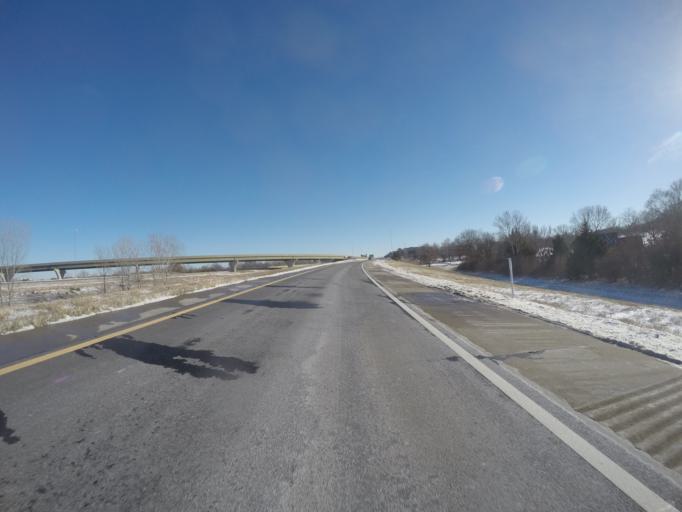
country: US
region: Kansas
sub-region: Shawnee County
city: Topeka
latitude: 39.0520
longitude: -95.7746
